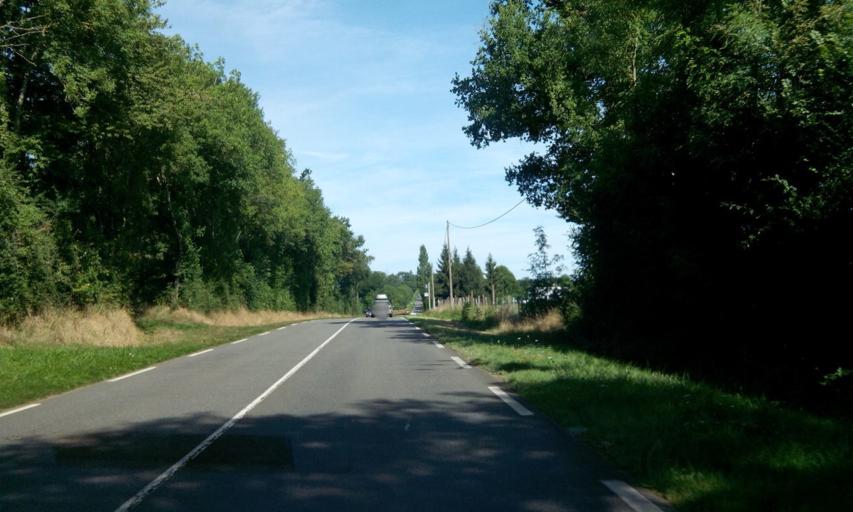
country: FR
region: Poitou-Charentes
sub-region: Departement de la Charente
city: Confolens
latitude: 45.9700
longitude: 0.6928
